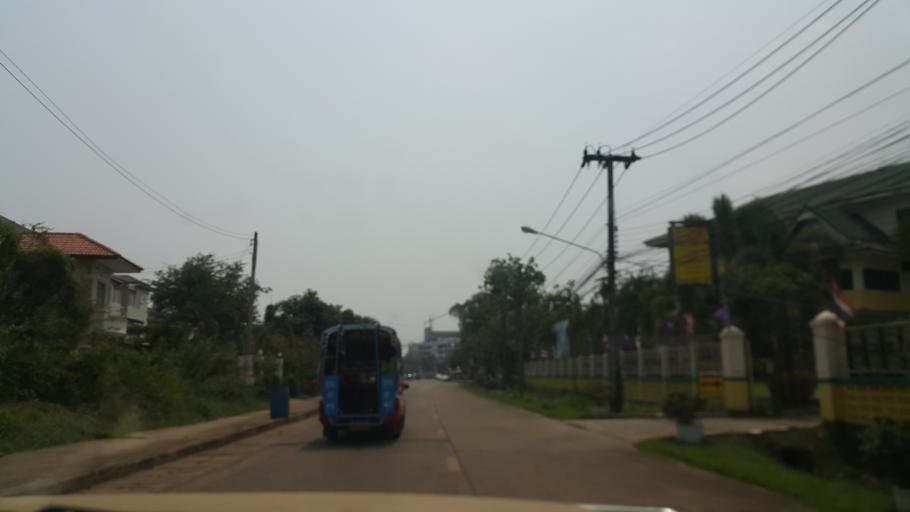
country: TH
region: Nakhon Phanom
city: Nakhon Phanom
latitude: 17.4185
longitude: 104.7765
